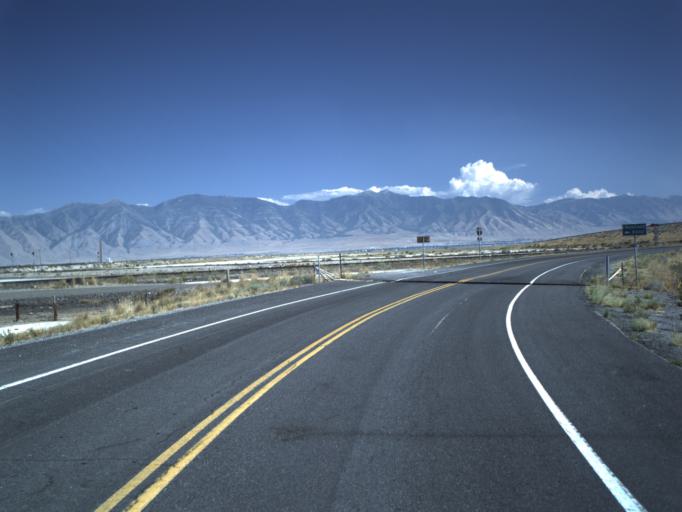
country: US
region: Utah
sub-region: Tooele County
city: Grantsville
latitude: 40.6867
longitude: -112.4434
